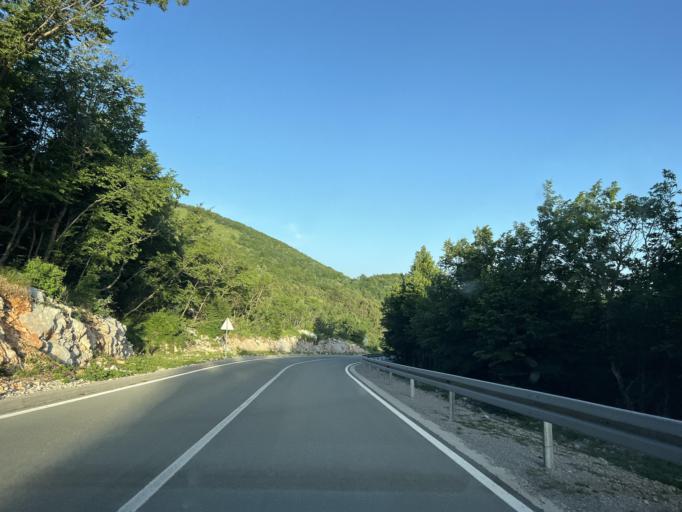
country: HR
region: Primorsko-Goranska
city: Skrljevo
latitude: 45.3917
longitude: 14.5591
